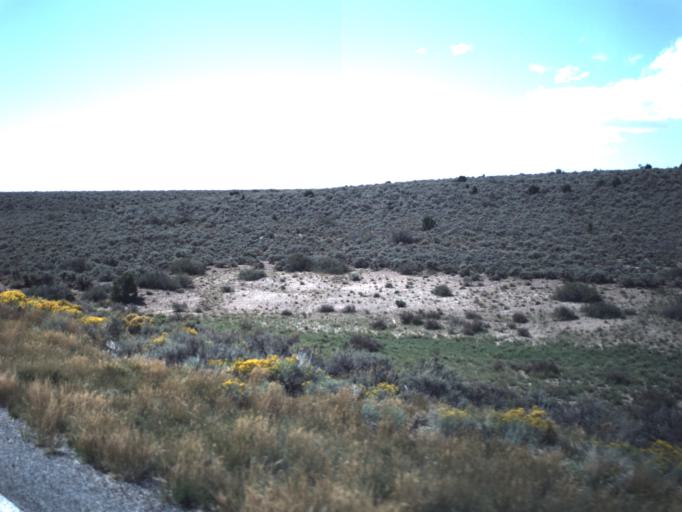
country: US
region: Utah
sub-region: Iron County
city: Parowan
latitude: 38.0709
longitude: -112.9613
